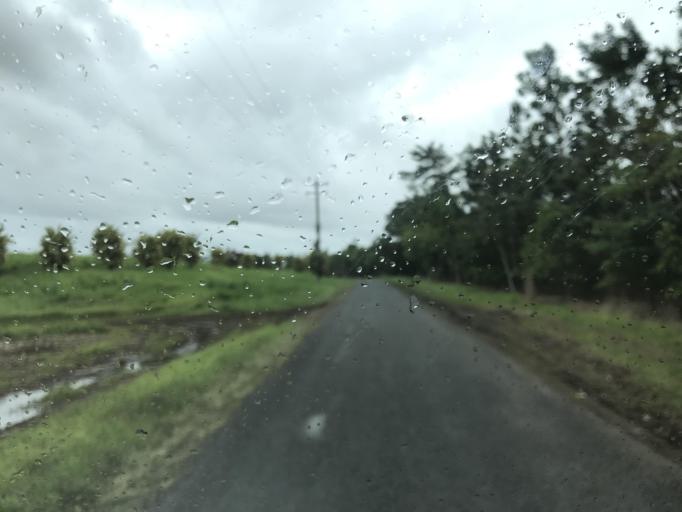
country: AU
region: Queensland
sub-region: Cassowary Coast
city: Innisfail
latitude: -17.4894
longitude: 145.9883
